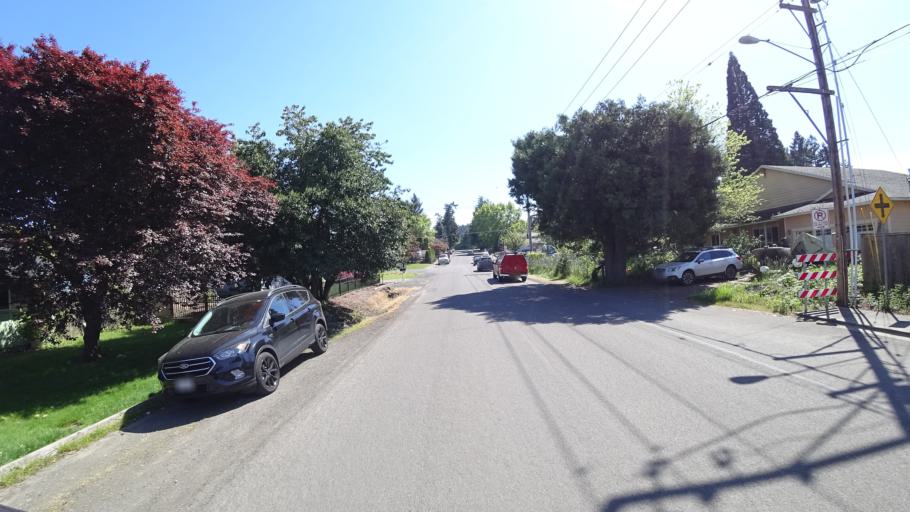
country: US
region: Oregon
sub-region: Washington County
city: Aloha
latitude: 45.4816
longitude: -122.8420
